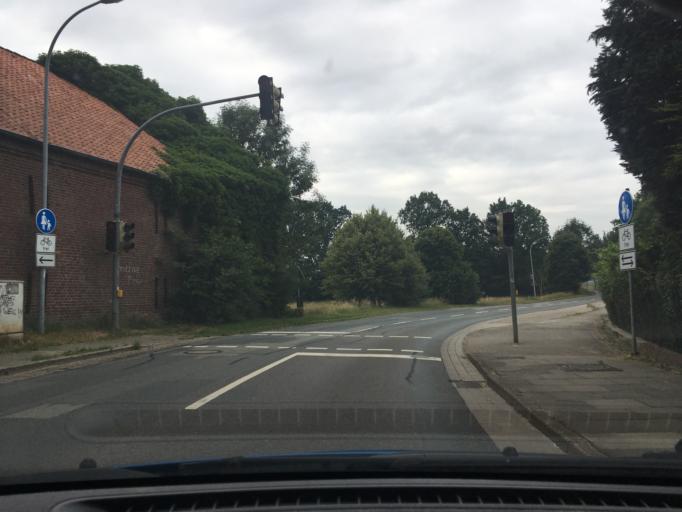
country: DE
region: Lower Saxony
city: Wenzendorf
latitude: 53.3480
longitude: 9.7561
